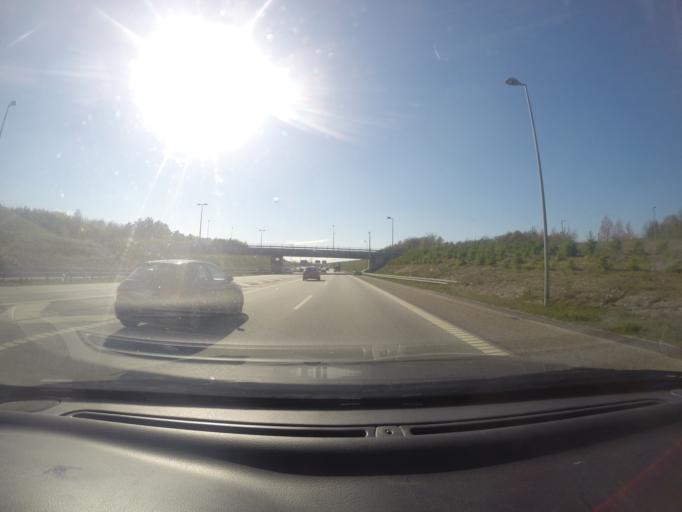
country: DK
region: Capital Region
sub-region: Rodovre Kommune
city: Rodovre
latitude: 55.6909
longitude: 12.4260
